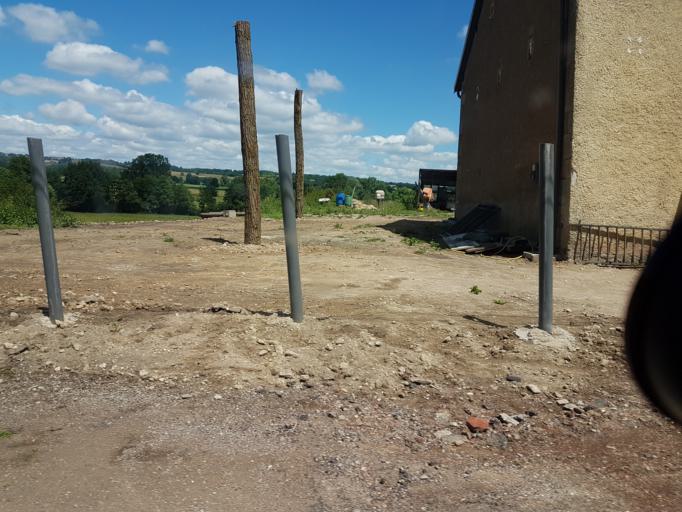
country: FR
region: Bourgogne
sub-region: Departement de Saone-et-Loire
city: Curgy
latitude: 47.0281
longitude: 4.4307
